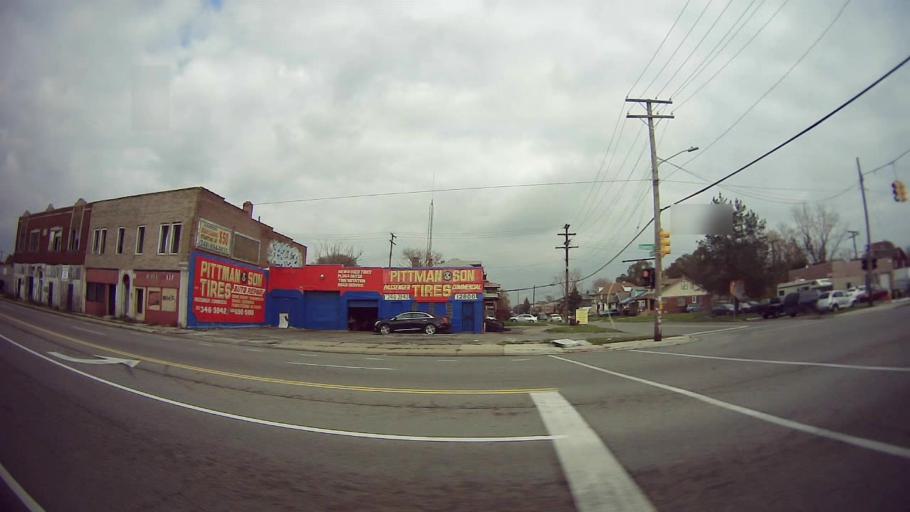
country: US
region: Michigan
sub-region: Wayne County
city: Highland Park
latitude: 42.3903
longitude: -83.1203
